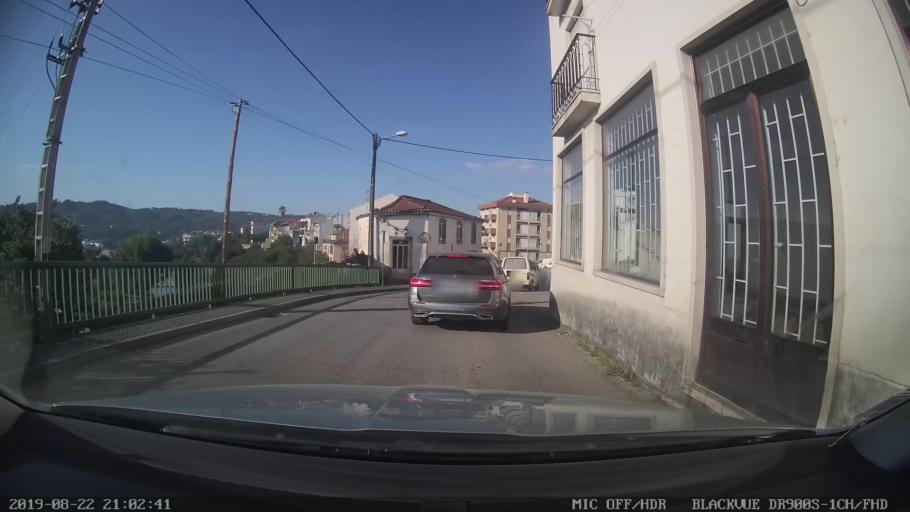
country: PT
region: Castelo Branco
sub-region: Serta
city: Serta
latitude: 39.8078
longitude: -8.0971
